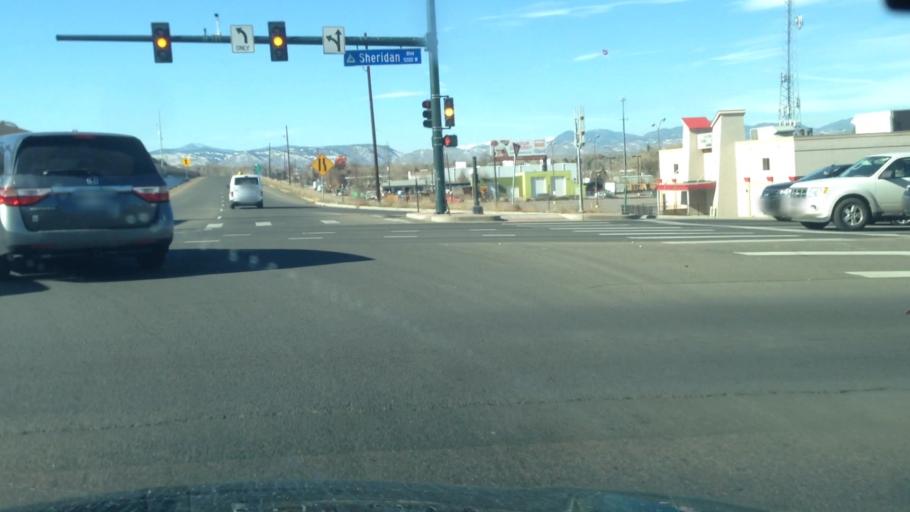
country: US
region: Colorado
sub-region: Jefferson County
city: Edgewater
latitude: 39.7261
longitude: -105.0531
